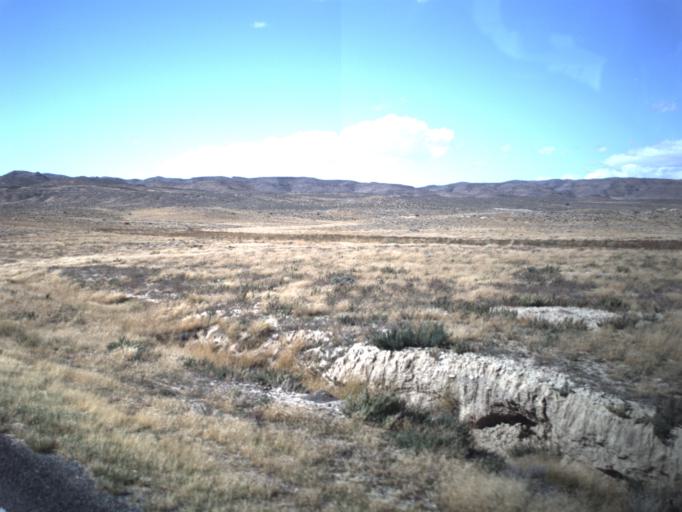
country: US
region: Utah
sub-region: Millard County
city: Fillmore
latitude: 38.8969
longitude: -112.8241
